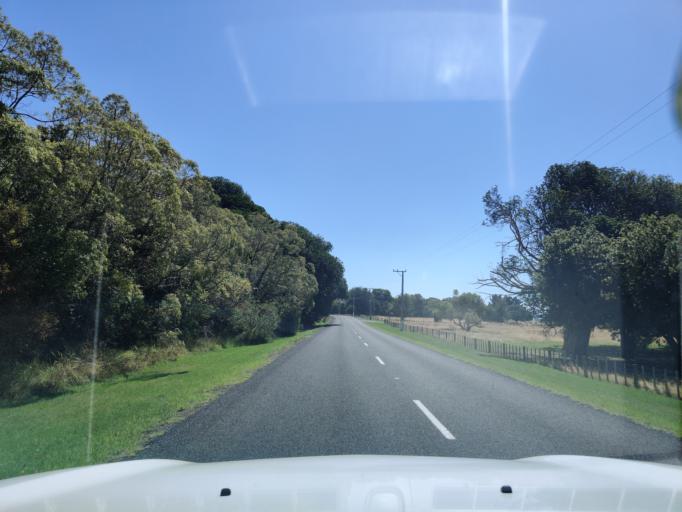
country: NZ
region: Waikato
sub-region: Thames-Coromandel District
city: Thames
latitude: -37.0409
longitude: 175.2954
